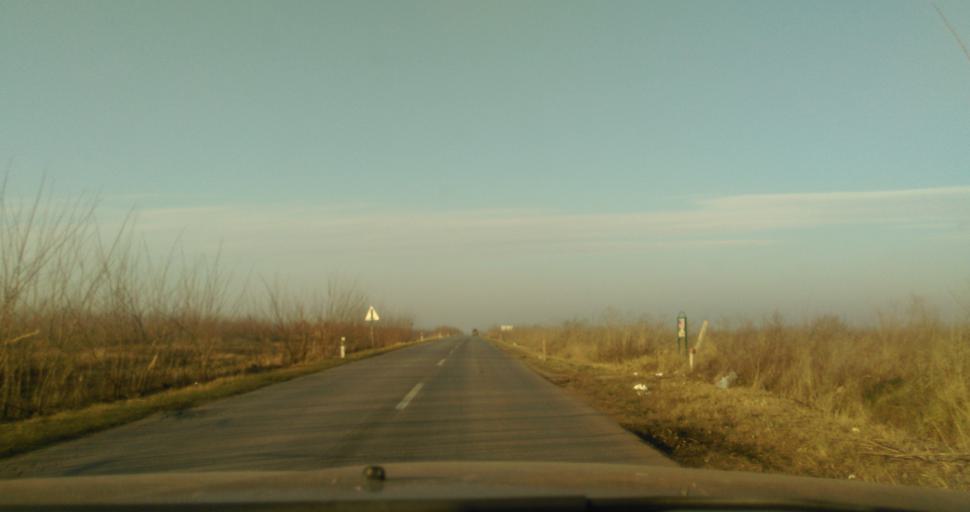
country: RS
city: Curug
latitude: 45.4757
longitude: 20.0435
